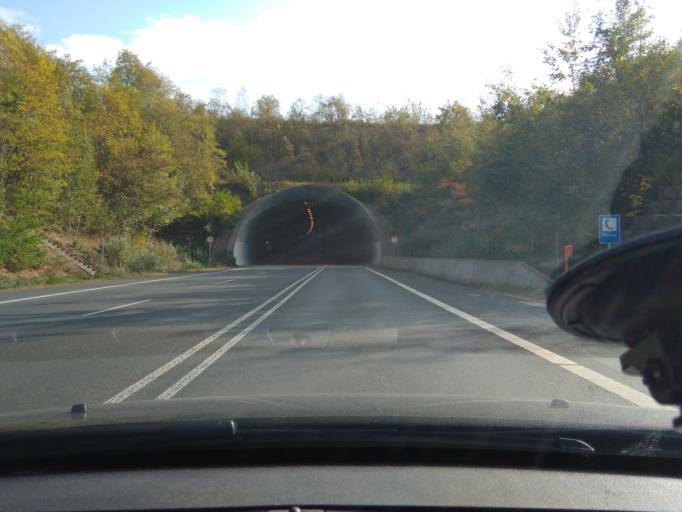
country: DE
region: Saxony
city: Meissen
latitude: 51.1674
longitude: 13.4598
